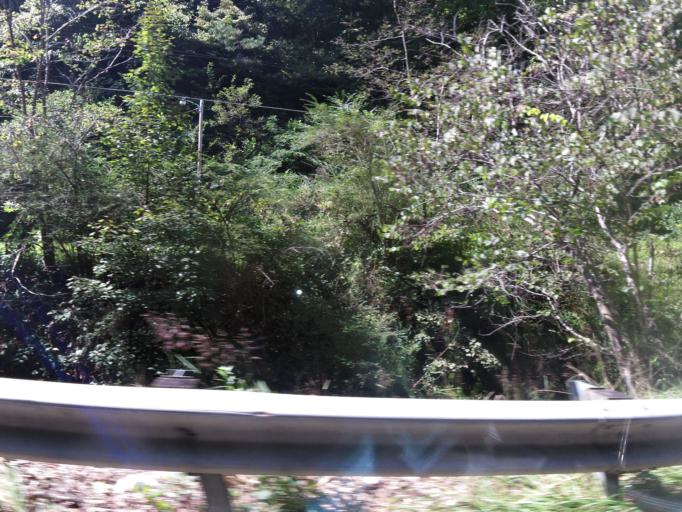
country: US
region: Kentucky
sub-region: Leslie County
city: Hyden
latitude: 37.1221
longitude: -83.3820
